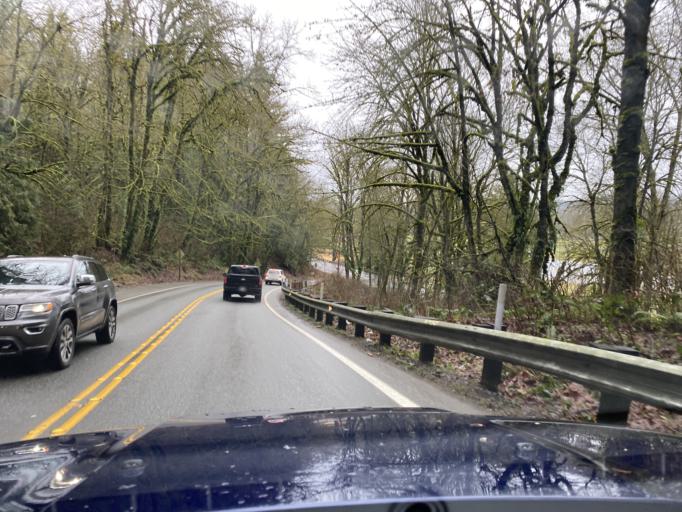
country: US
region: Washington
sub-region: King County
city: Union Hill-Novelty Hill
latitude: 47.7036
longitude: -122.0039
